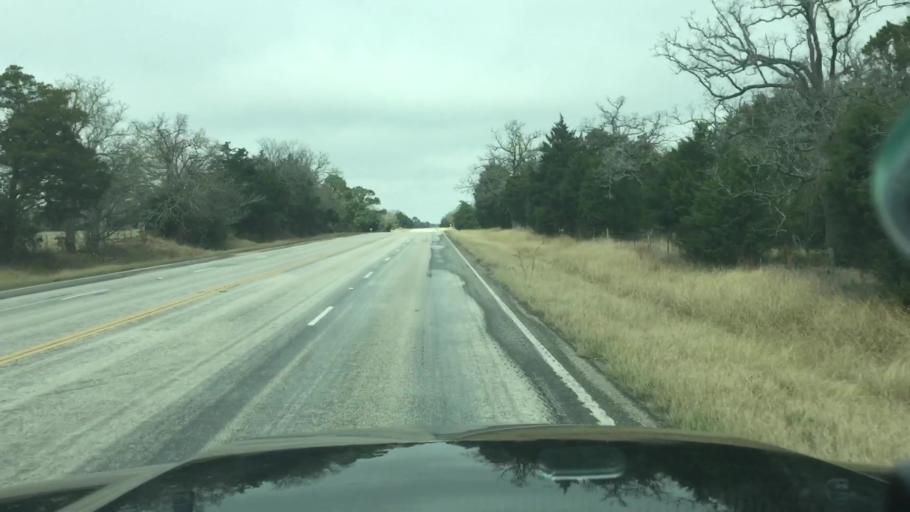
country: US
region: Texas
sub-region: Lee County
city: Giddings
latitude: 30.1087
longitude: -96.9149
